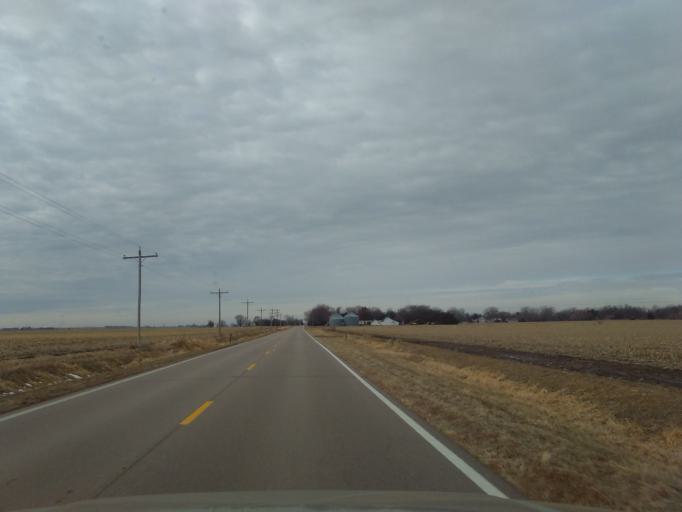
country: US
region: Nebraska
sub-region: Hall County
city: Grand Island
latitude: 40.7709
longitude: -98.4034
